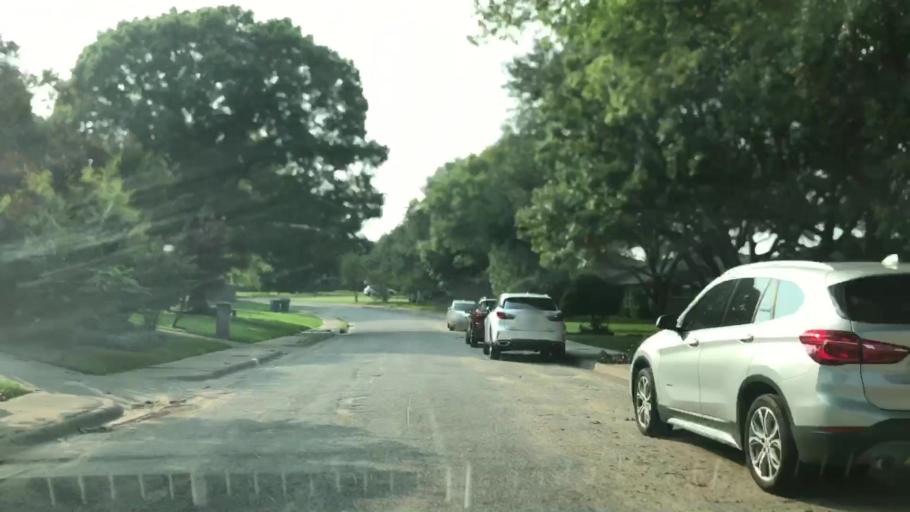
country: US
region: Texas
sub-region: Dallas County
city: Richardson
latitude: 32.9062
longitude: -96.7292
